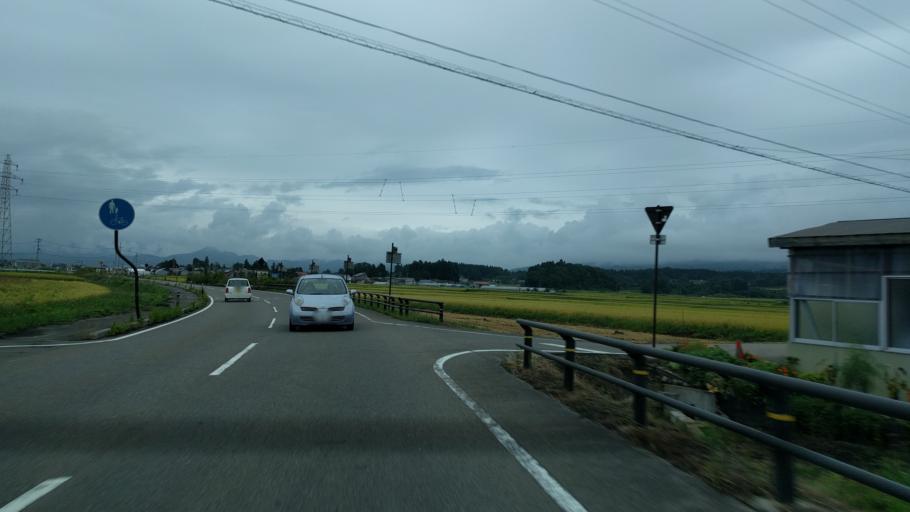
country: JP
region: Fukushima
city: Kitakata
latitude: 37.5930
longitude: 139.9123
